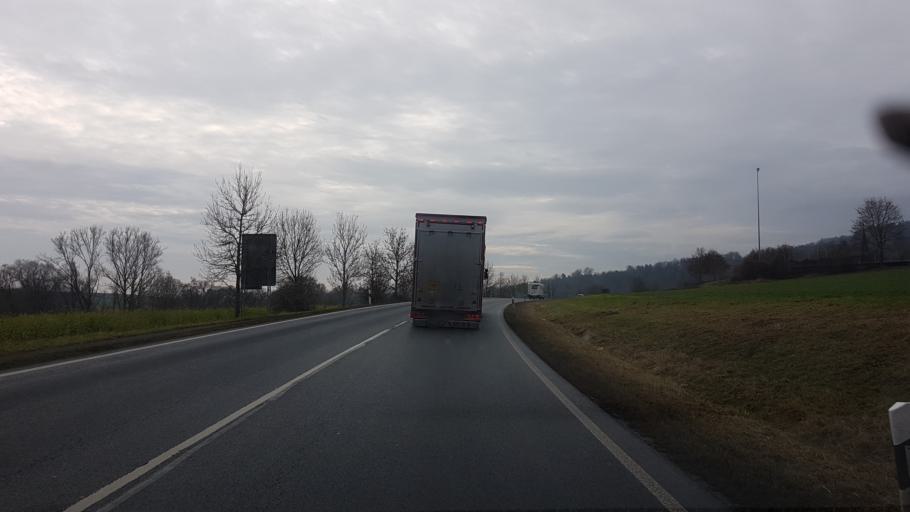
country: DE
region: Bavaria
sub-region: Regierungsbezirk Unterfranken
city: Rentweinsdorf
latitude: 50.0822
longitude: 10.7941
